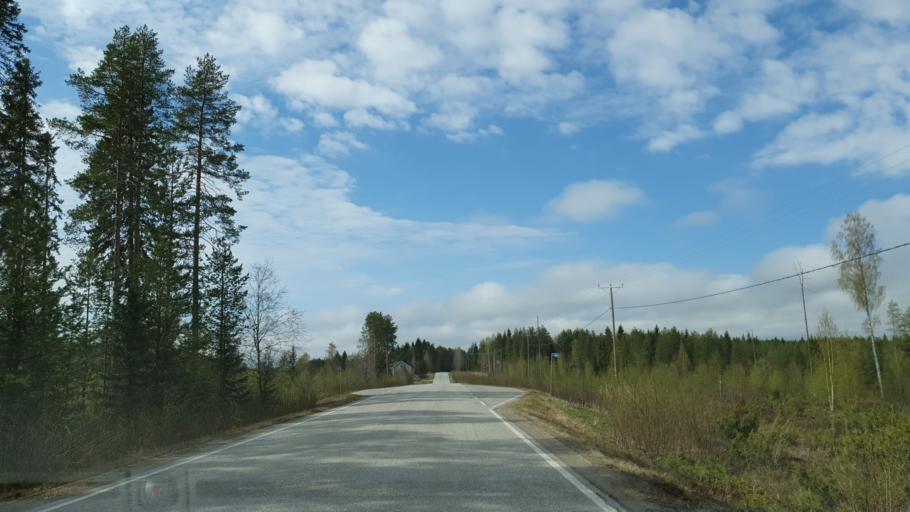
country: FI
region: Kainuu
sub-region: Kehys-Kainuu
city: Kuhmo
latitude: 64.1218
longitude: 29.6664
